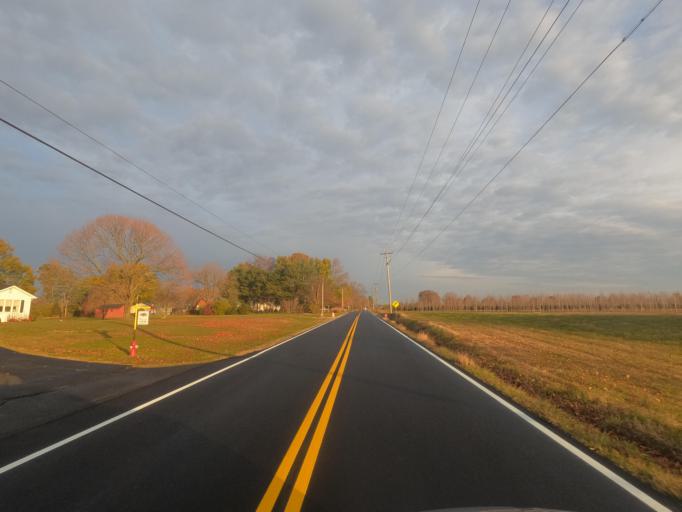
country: US
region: Delaware
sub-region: New Castle County
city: Townsend
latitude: 39.2755
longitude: -75.8376
